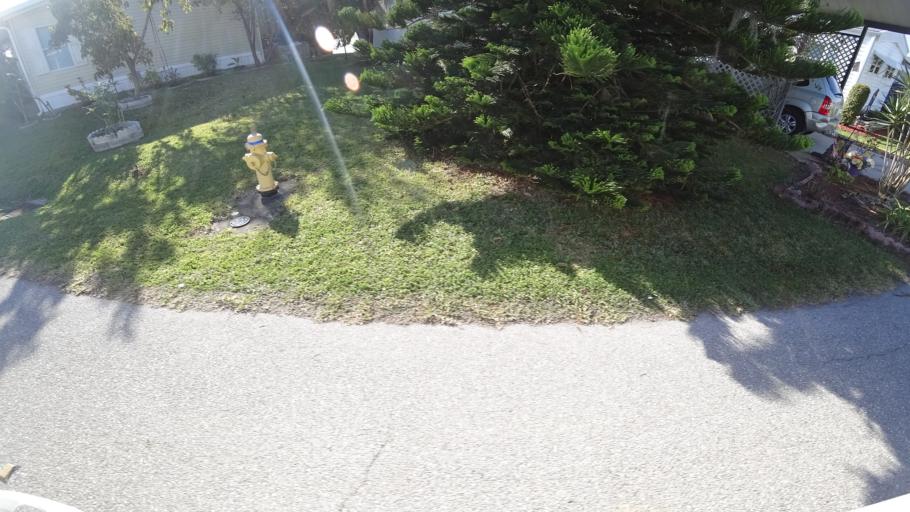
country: US
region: Florida
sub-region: Manatee County
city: Ellenton
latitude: 27.5269
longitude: -82.5233
